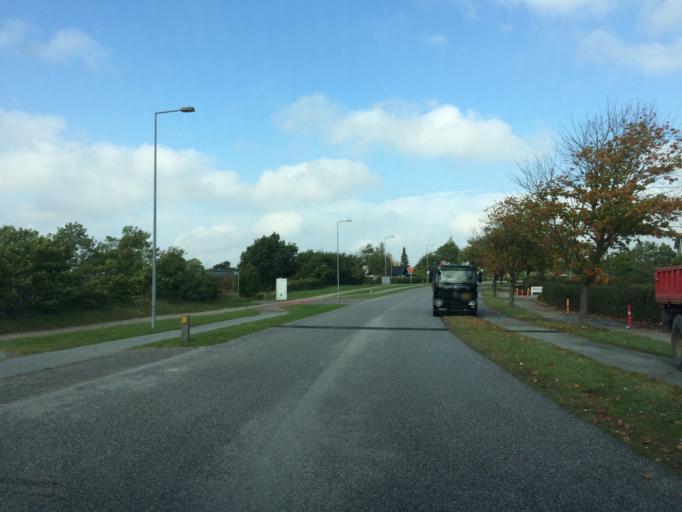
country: DK
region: Central Jutland
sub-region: Skive Kommune
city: Skive
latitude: 56.5505
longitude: 9.0154
